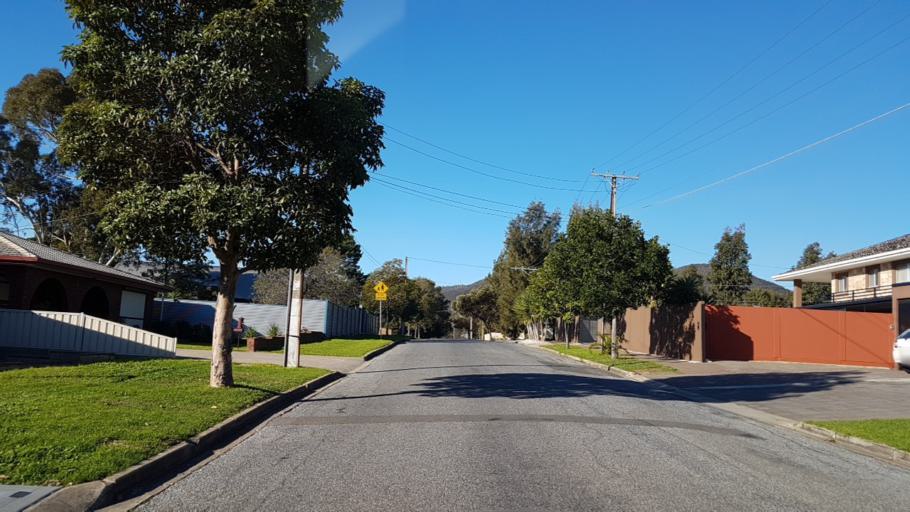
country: AU
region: South Australia
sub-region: Campbelltown
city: Athelstone
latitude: -34.8777
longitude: 138.6865
